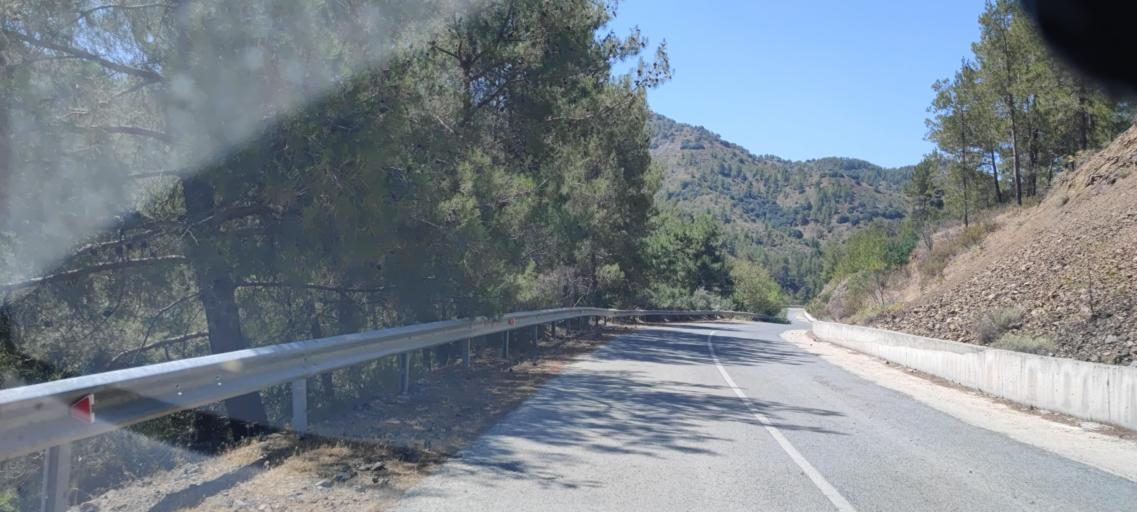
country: CY
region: Lefkosia
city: Kakopetria
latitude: 34.9289
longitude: 32.8038
